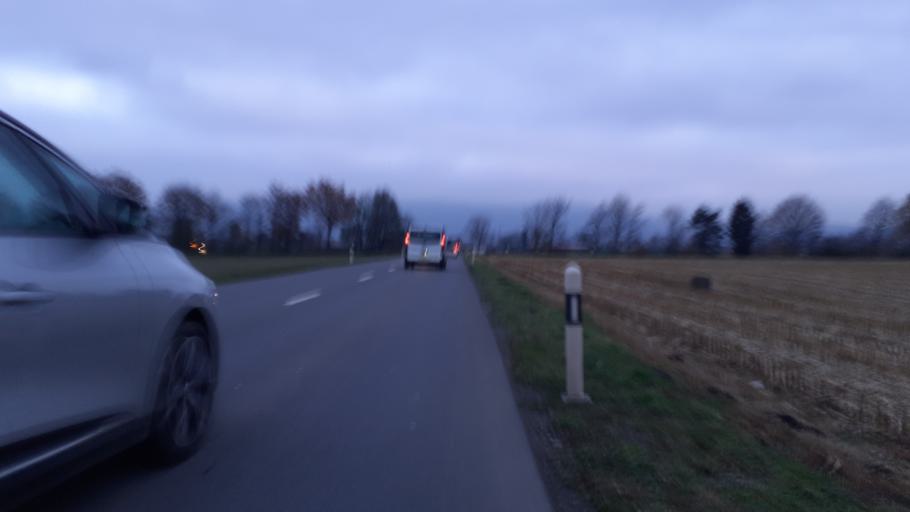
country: AT
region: Vorarlberg
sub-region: Politischer Bezirk Feldkirch
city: Mader
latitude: 47.3624
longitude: 9.5962
